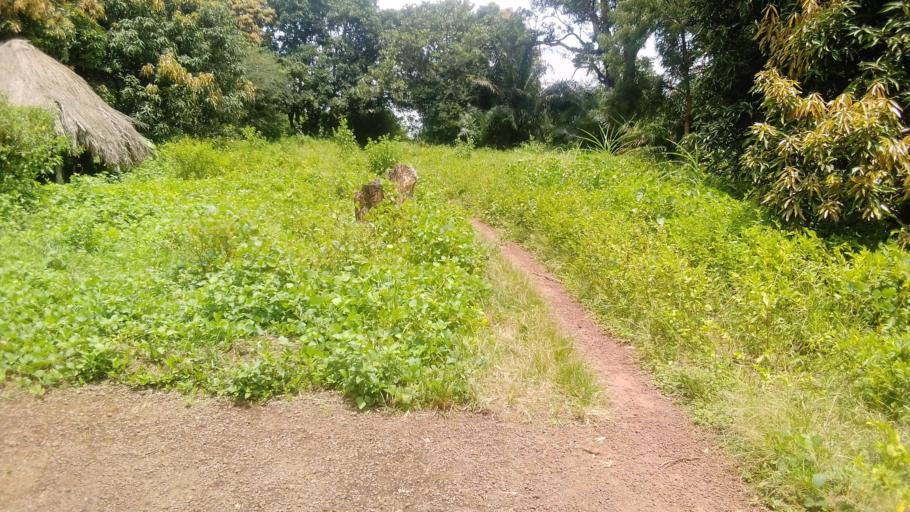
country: SL
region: Northern Province
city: Makeni
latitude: 9.0543
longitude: -12.1862
